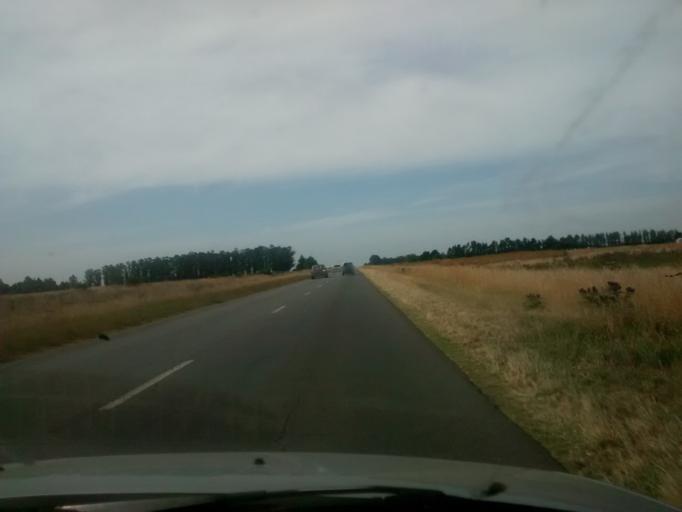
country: AR
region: Buenos Aires
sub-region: Partido de Loberia
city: Loberia
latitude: -38.1324
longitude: -58.7530
